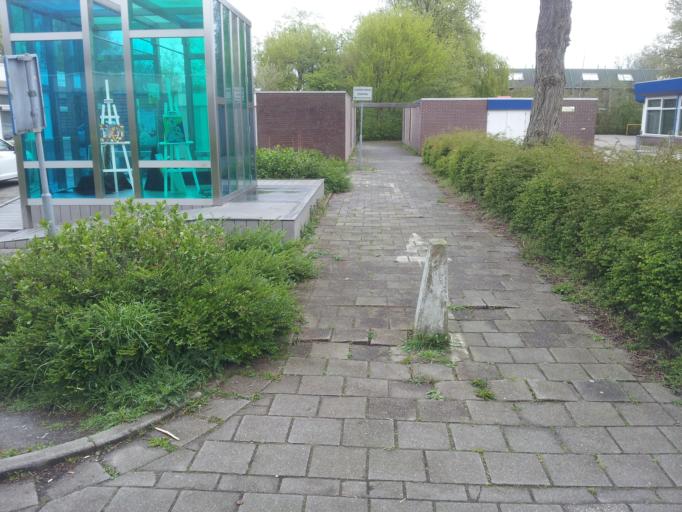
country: NL
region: South Holland
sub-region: Gemeente Zoetermeer
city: Zoetermeer
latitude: 52.0692
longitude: 4.4711
